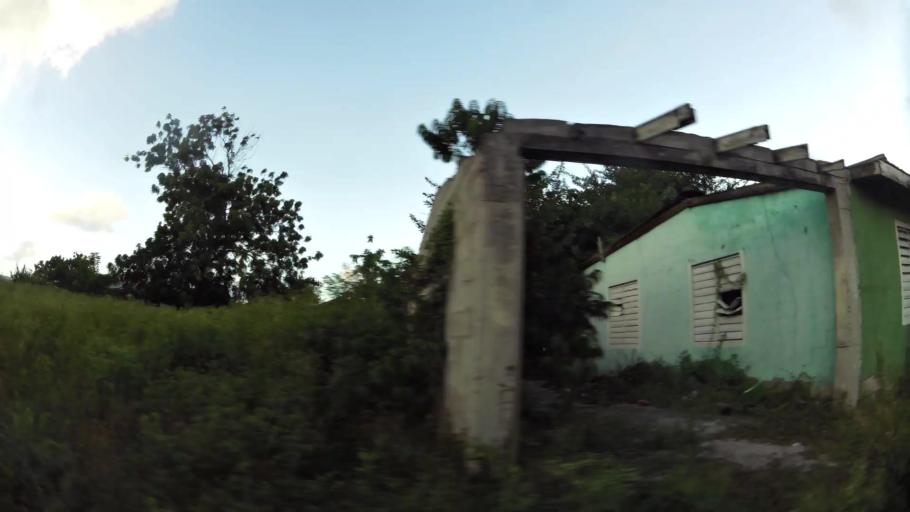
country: AG
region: Saint John
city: Saint John's
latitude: 17.1344
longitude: -61.8425
